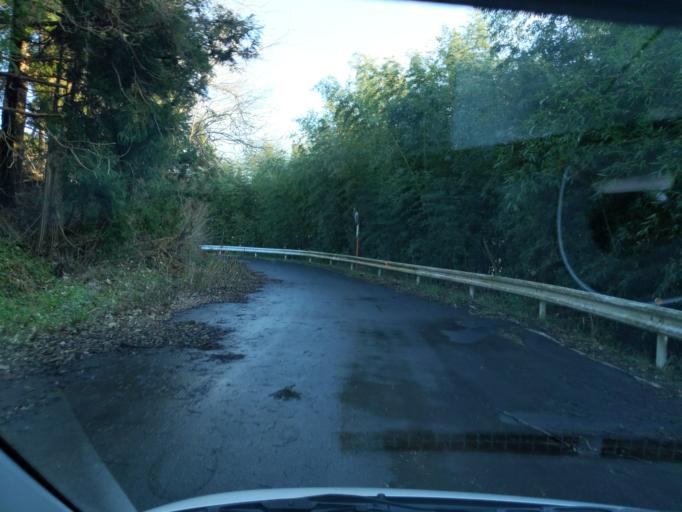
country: JP
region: Miyagi
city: Wakuya
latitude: 38.6960
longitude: 141.1245
